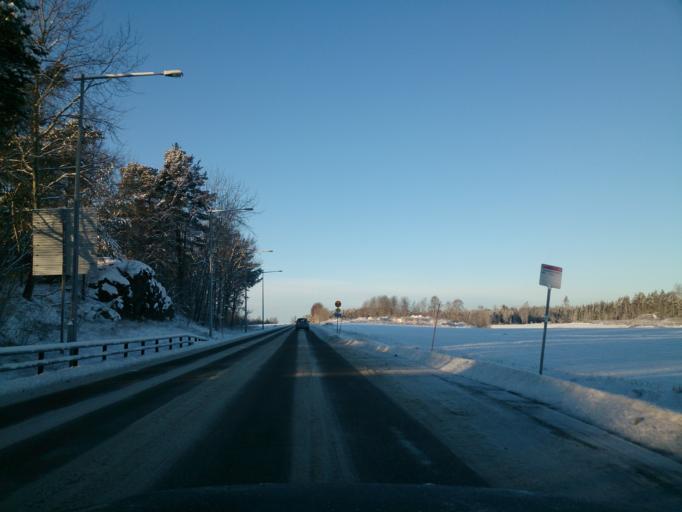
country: SE
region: OEstergoetland
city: Lindo
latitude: 58.5810
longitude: 16.3127
